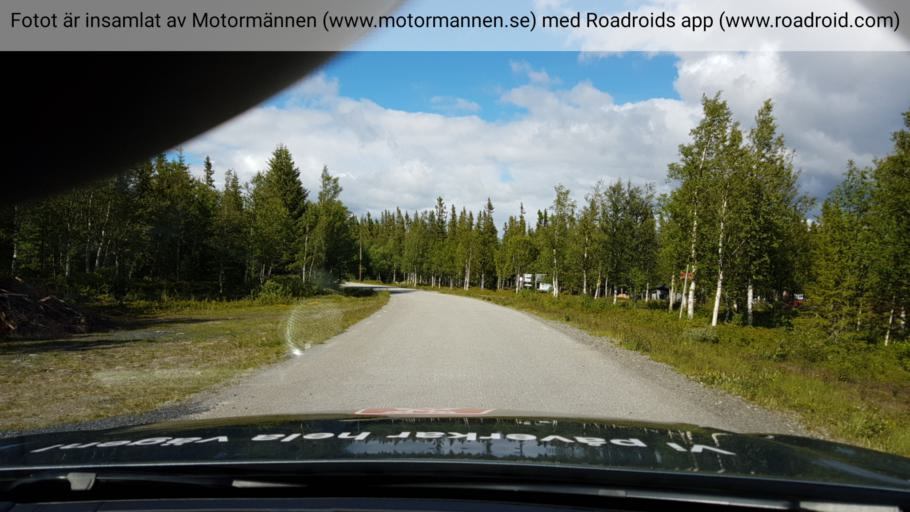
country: SE
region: Jaemtland
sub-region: Bergs Kommun
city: Hoverberg
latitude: 63.0040
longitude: 13.9453
